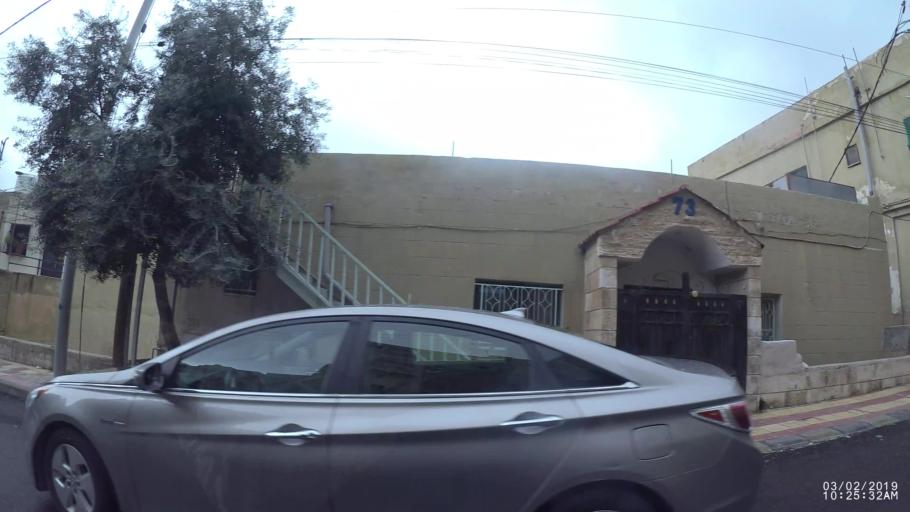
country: JO
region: Amman
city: Amman
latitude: 31.9488
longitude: 35.9174
